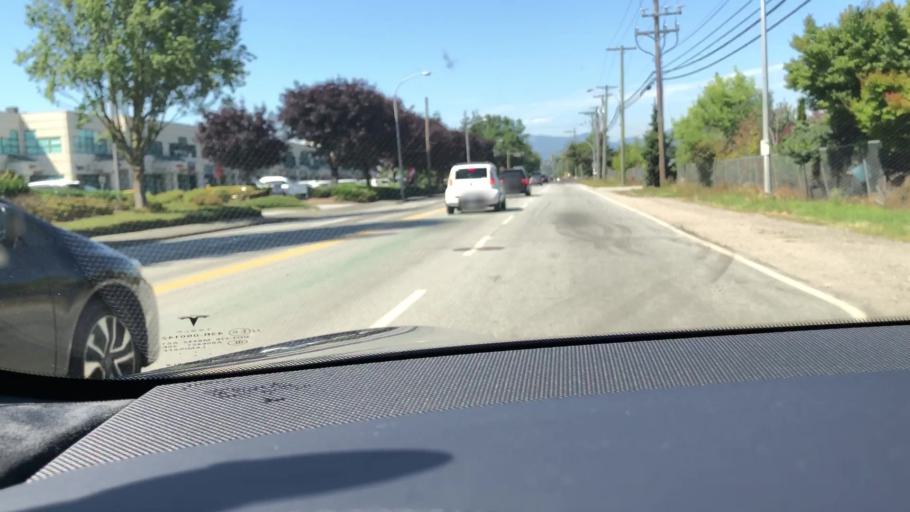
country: CA
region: British Columbia
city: Richmond
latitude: 49.1830
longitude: -123.0691
